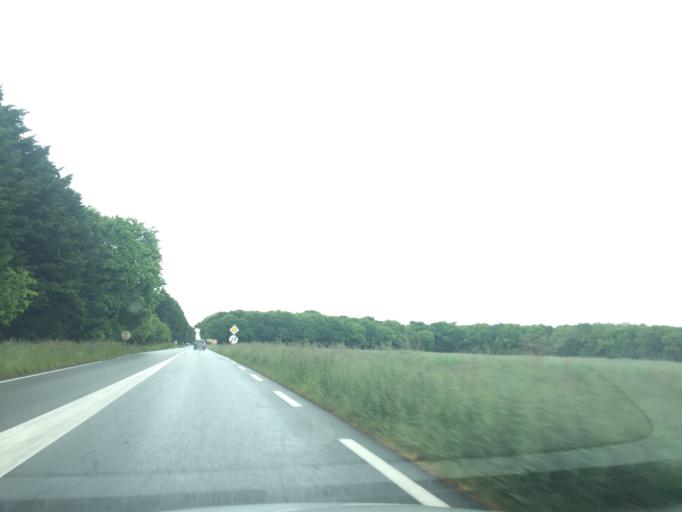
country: FR
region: Brittany
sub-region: Departement des Cotes-d'Armor
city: Ploubalay
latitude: 48.5940
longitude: -2.0998
